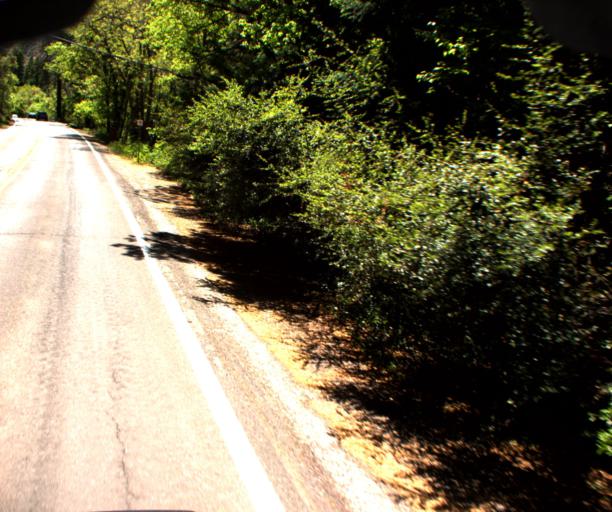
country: US
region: Arizona
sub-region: Coconino County
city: Kachina Village
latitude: 34.9886
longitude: -111.7443
